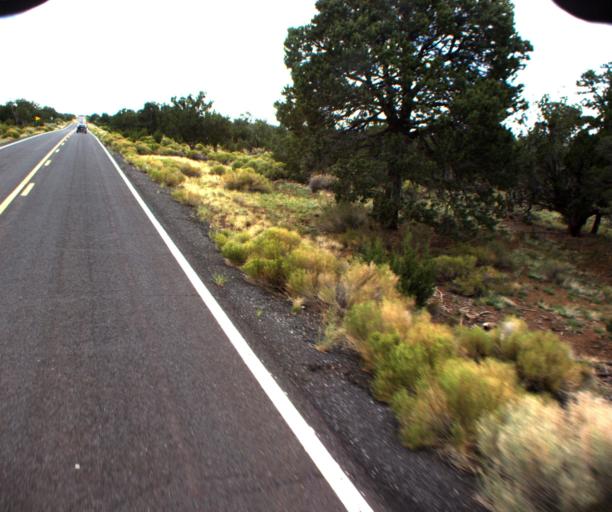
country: US
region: Arizona
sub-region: Coconino County
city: Parks
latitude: 35.5448
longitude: -111.8573
